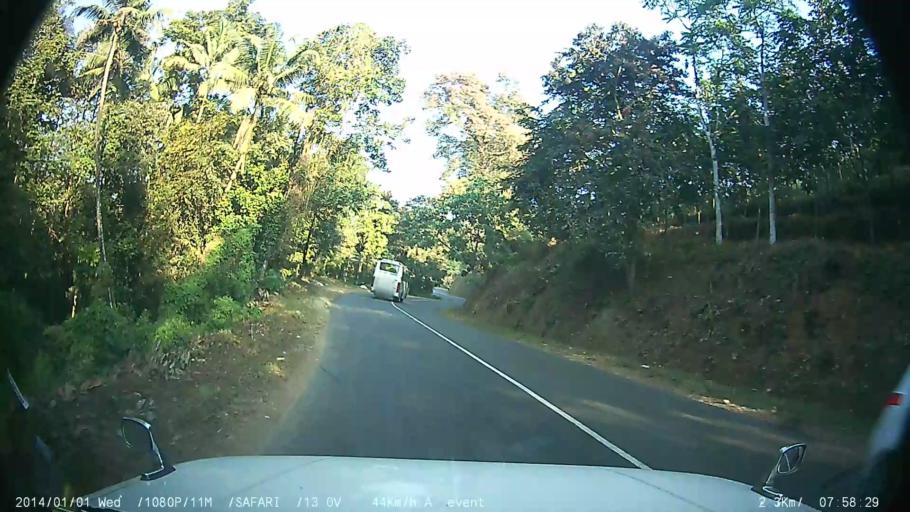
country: IN
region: Kerala
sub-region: Ernakulam
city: Muvattupuzha
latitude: 9.9220
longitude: 76.5840
